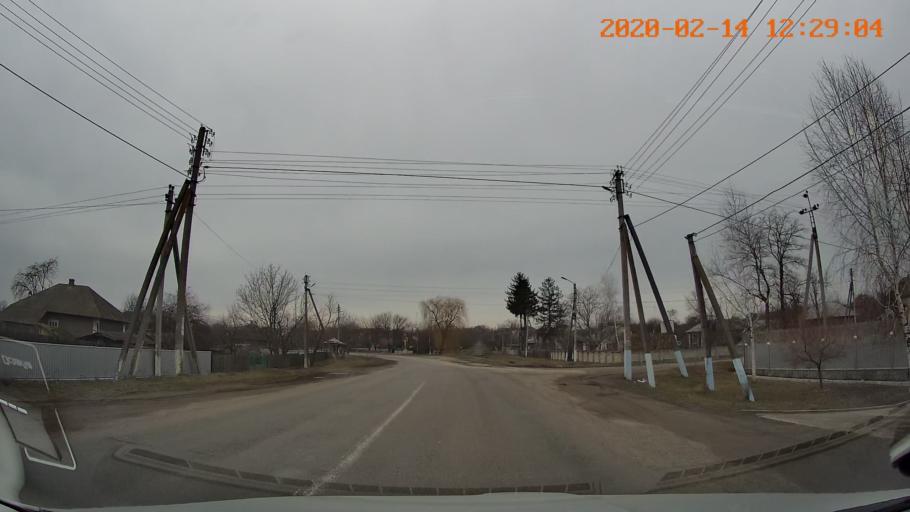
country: RO
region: Botosani
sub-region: Comuna Darabani
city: Bajura
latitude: 48.2589
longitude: 26.5872
